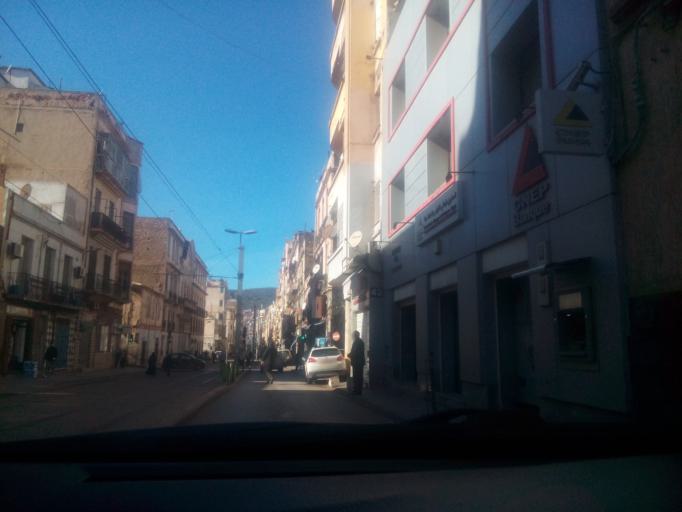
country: DZ
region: Oran
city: Oran
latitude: 35.6998
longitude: -0.6399
